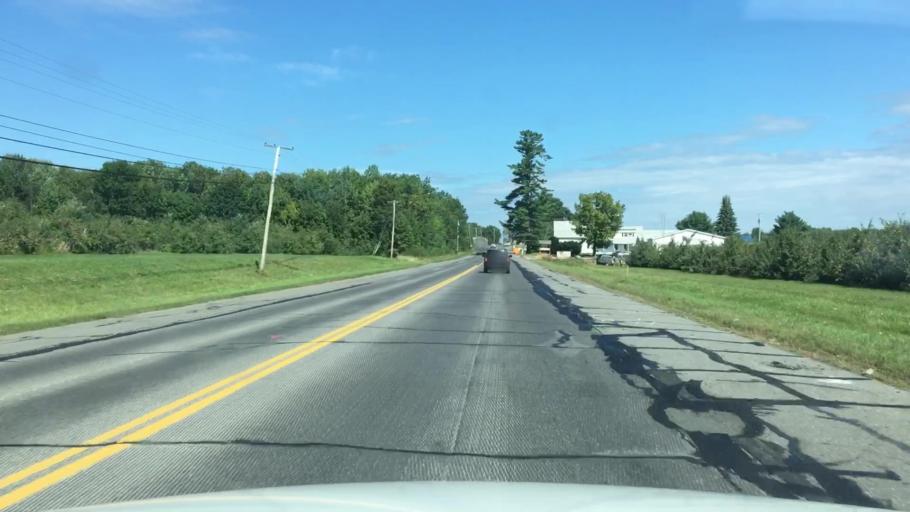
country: US
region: Maine
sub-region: Penobscot County
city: Newport
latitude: 44.8548
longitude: -69.2832
